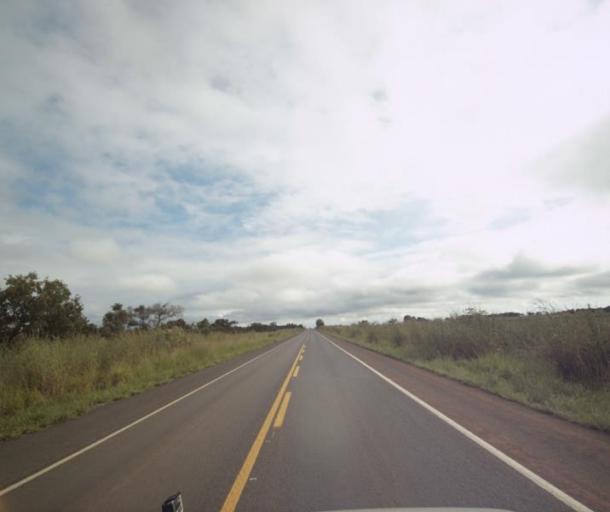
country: BR
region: Goias
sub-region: Padre Bernardo
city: Padre Bernardo
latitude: -15.3630
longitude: -48.6462
